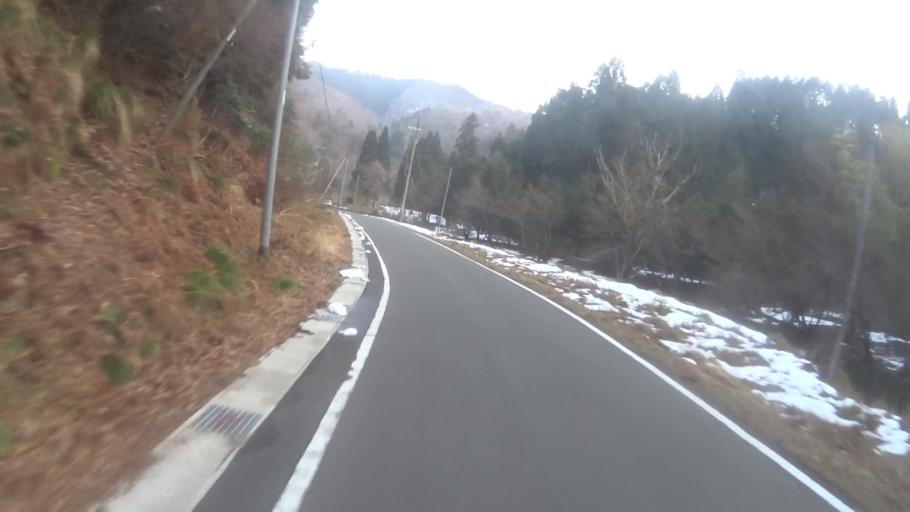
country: JP
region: Kyoto
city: Maizuru
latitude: 35.4330
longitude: 135.4767
